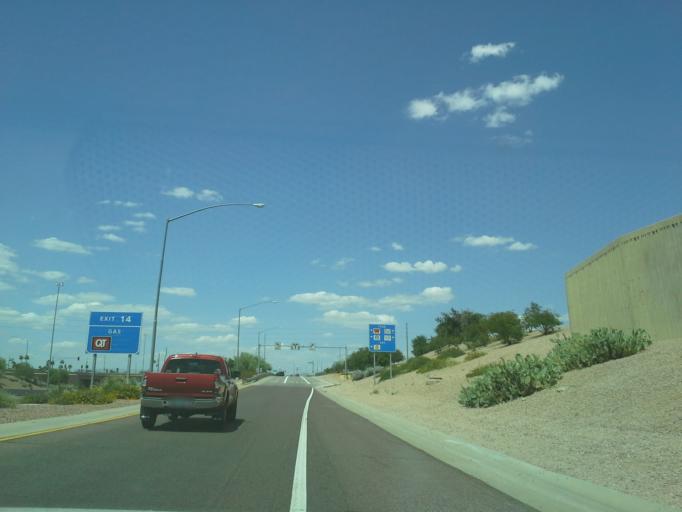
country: US
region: Arizona
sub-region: Maricopa County
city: Paradise Valley
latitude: 33.6377
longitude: -112.0036
